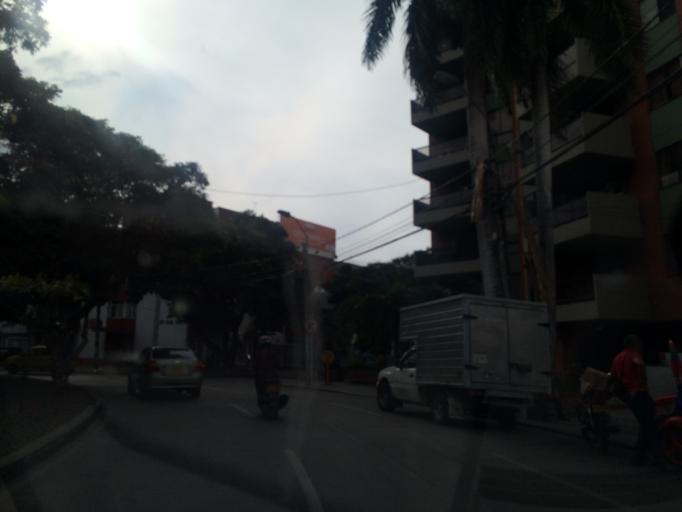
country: CO
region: Valle del Cauca
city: Cali
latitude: 3.4650
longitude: -76.5261
